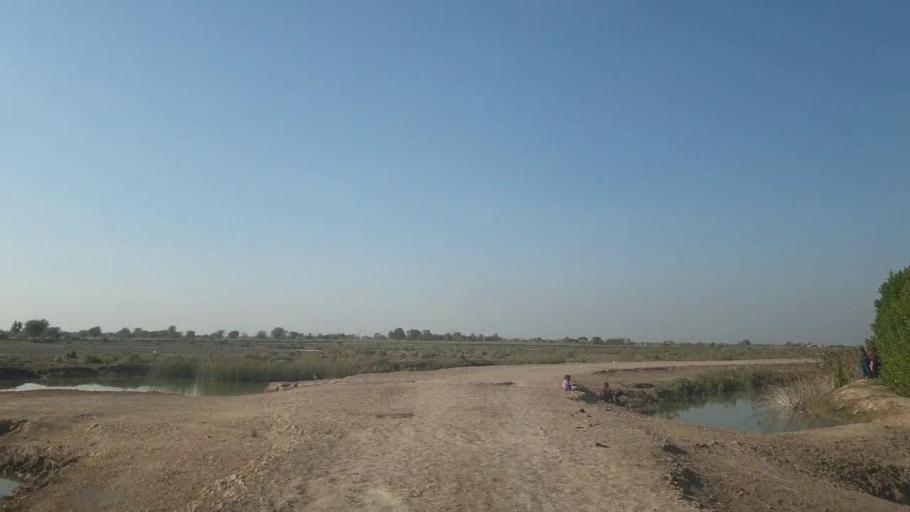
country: PK
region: Sindh
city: Mirwah Gorchani
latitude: 25.4252
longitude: 69.1294
